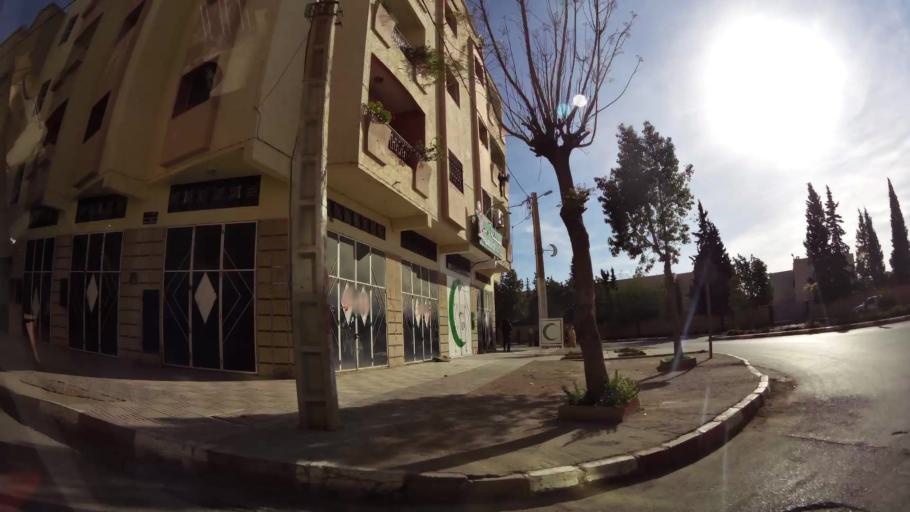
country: MA
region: Oriental
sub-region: Oujda-Angad
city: Oujda
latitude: 34.6715
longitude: -1.8995
